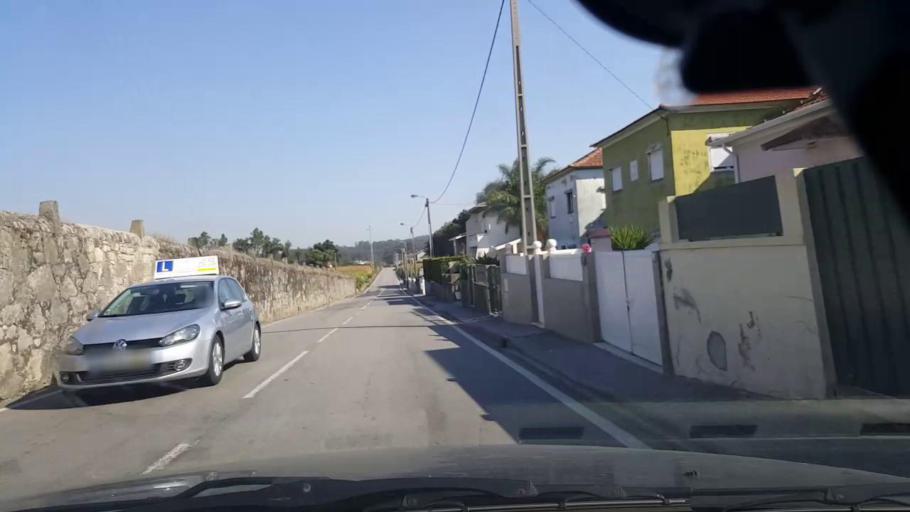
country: PT
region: Porto
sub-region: Vila do Conde
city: Arvore
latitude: 41.3420
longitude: -8.6808
